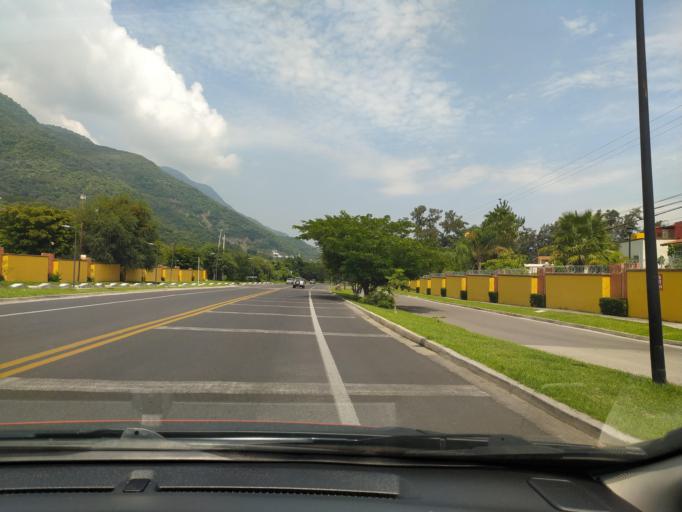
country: MX
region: Jalisco
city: Jocotepec
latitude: 20.2942
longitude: -103.3856
